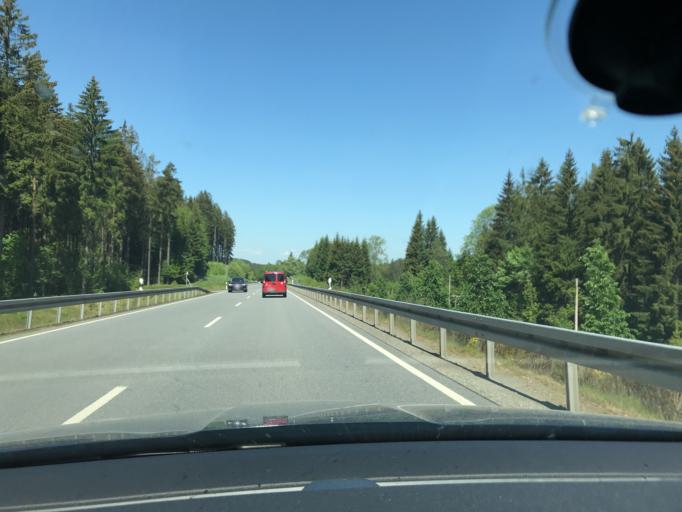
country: DE
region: Saxony
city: Elterlein
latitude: 50.6062
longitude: 12.8491
